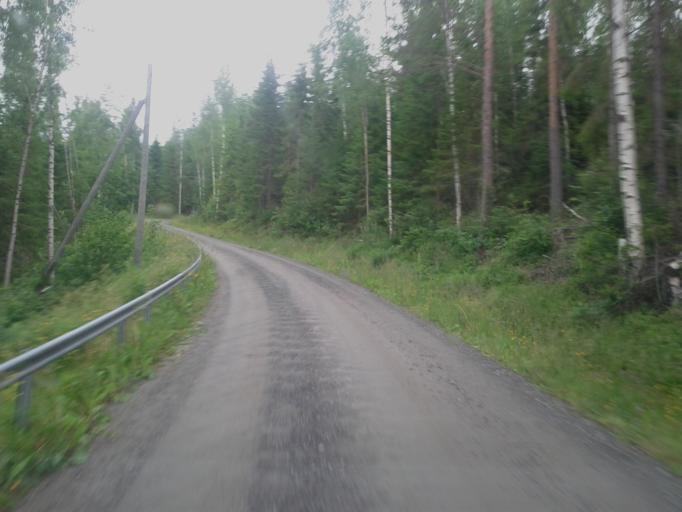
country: SE
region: Vaesternorrland
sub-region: OErnskoeldsviks Kommun
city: Bjasta
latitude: 63.0709
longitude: 18.4305
